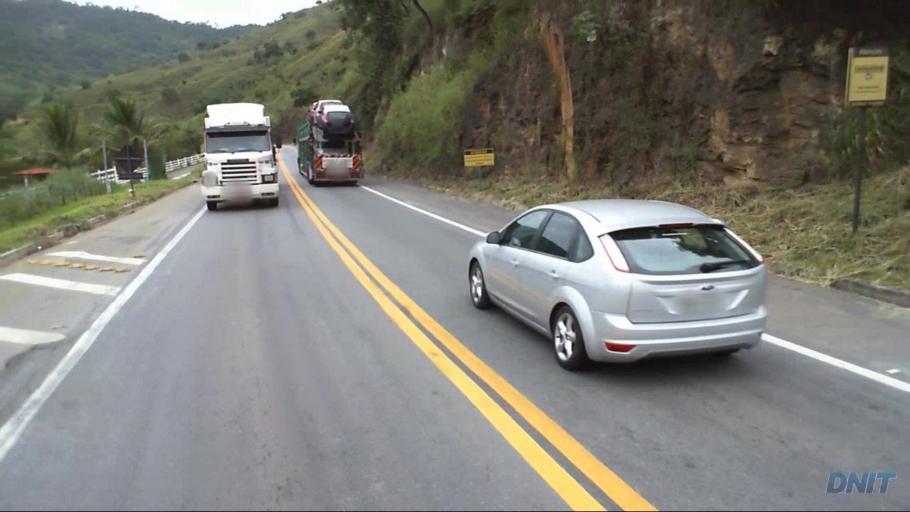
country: BR
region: Minas Gerais
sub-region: Timoteo
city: Timoteo
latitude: -19.6169
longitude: -42.7821
